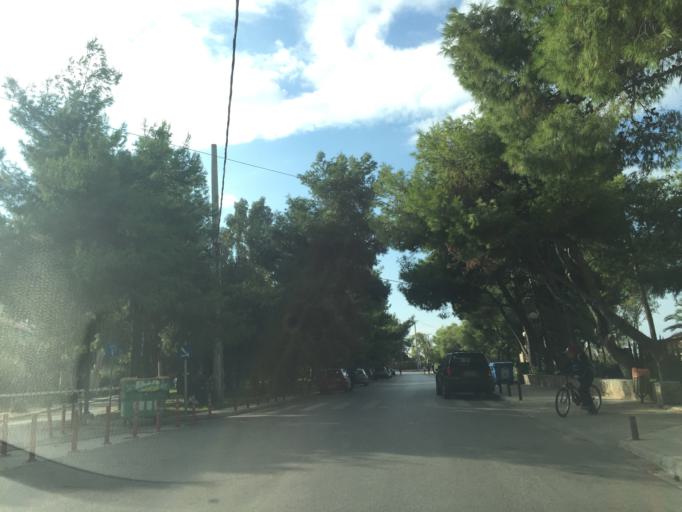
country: GR
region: Attica
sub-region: Nomarchia Anatolikis Attikis
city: Vouliagmeni
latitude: 37.8255
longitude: 23.7707
